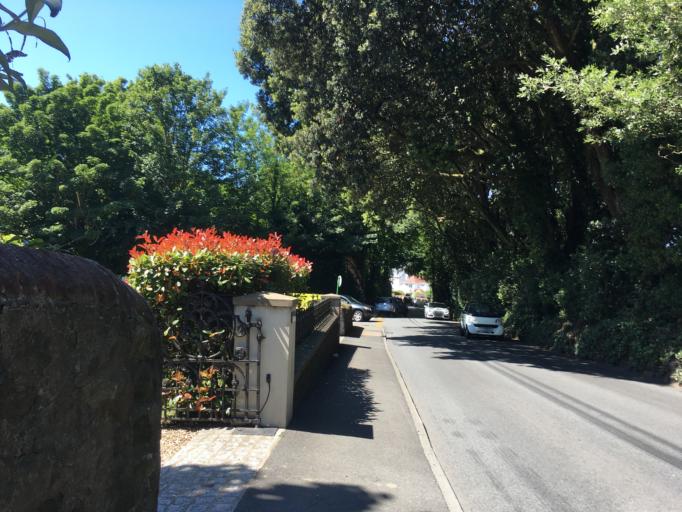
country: GG
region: St Peter Port
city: Saint Peter Port
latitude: 49.4577
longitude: -2.5522
